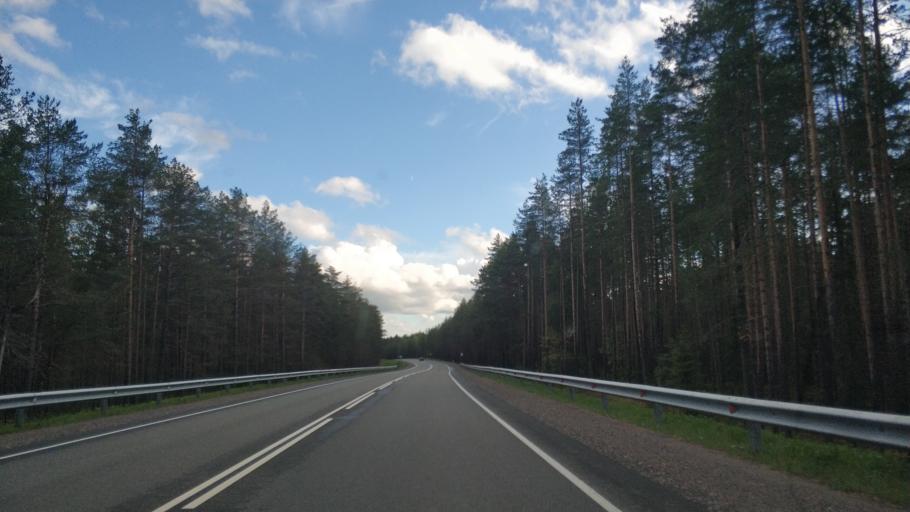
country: RU
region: Leningrad
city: Priozersk
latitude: 60.9893
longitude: 30.1834
